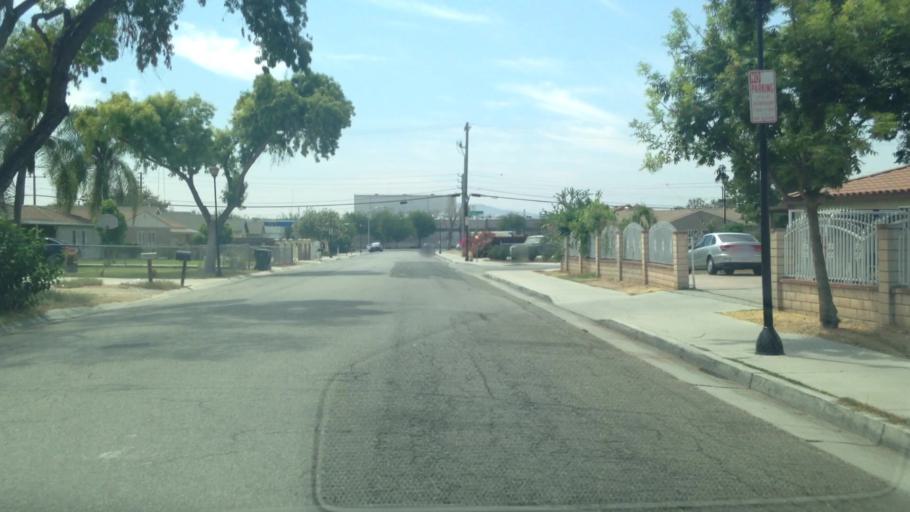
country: US
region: California
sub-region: Riverside County
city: Pedley
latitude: 33.9484
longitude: -117.4621
